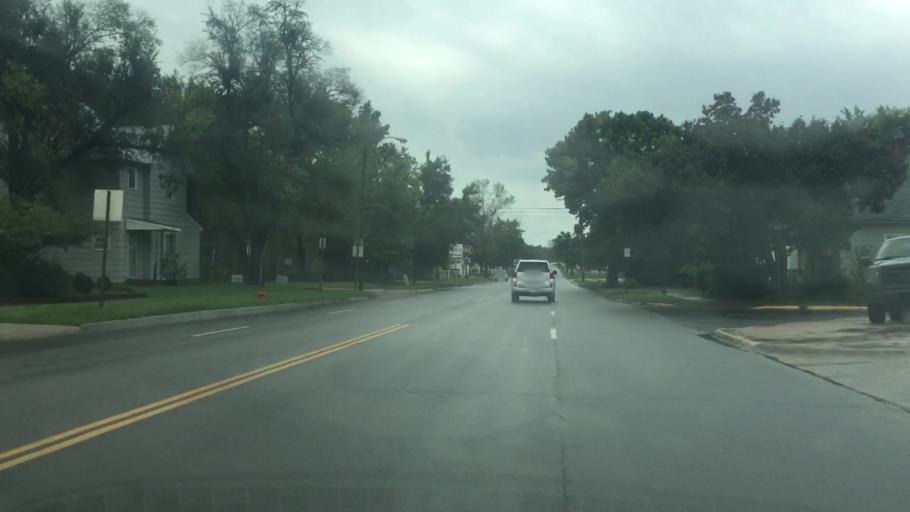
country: US
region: Kansas
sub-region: Allen County
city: Iola
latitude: 37.9205
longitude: -95.4091
